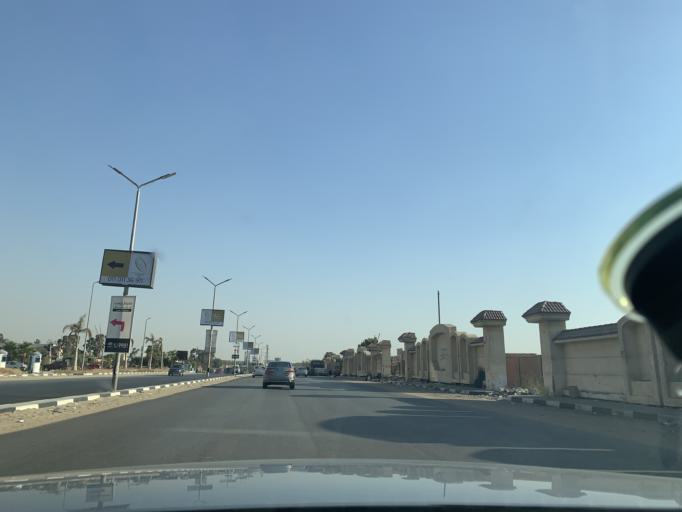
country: EG
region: Muhafazat al Qahirah
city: Cairo
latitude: 30.0321
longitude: 31.3545
